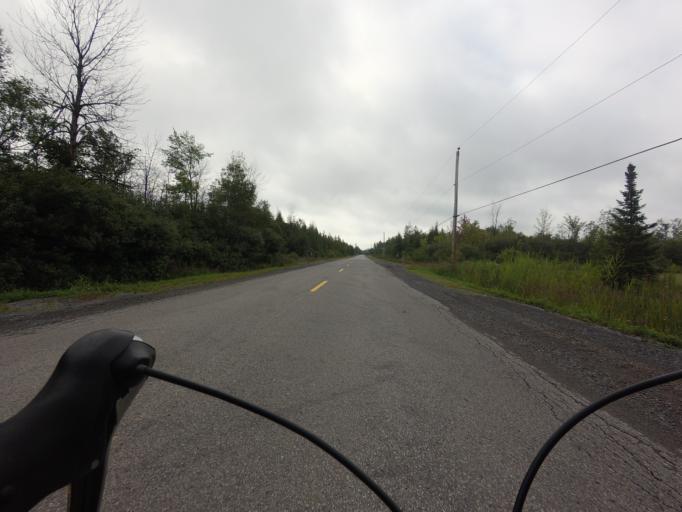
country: CA
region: Ontario
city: Bells Corners
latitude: 45.0747
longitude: -75.7377
